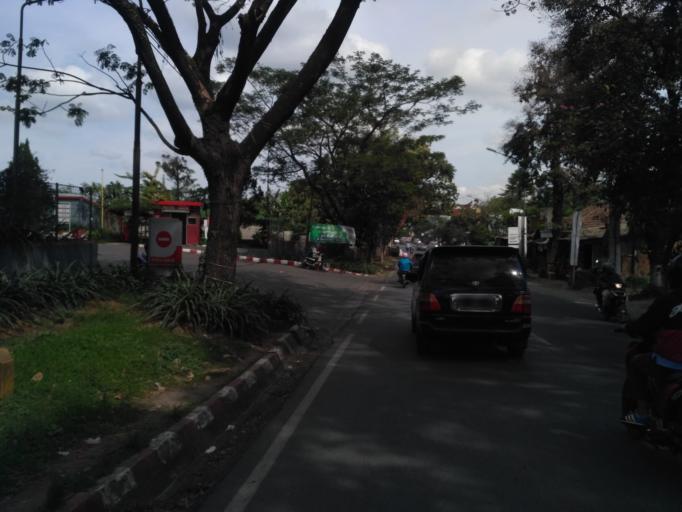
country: ID
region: East Java
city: Watudakon
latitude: -8.0311
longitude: 112.6269
